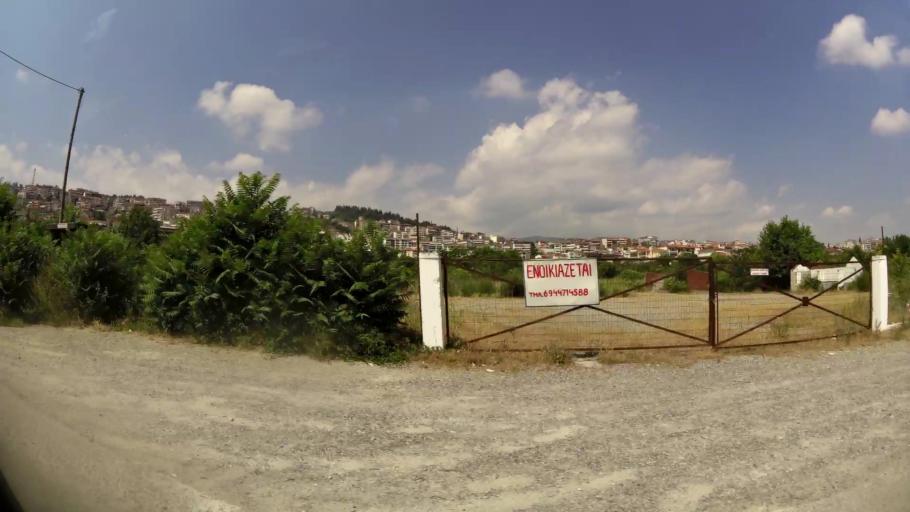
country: GR
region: Central Macedonia
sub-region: Nomos Imathias
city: Veroia
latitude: 40.5162
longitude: 22.2122
